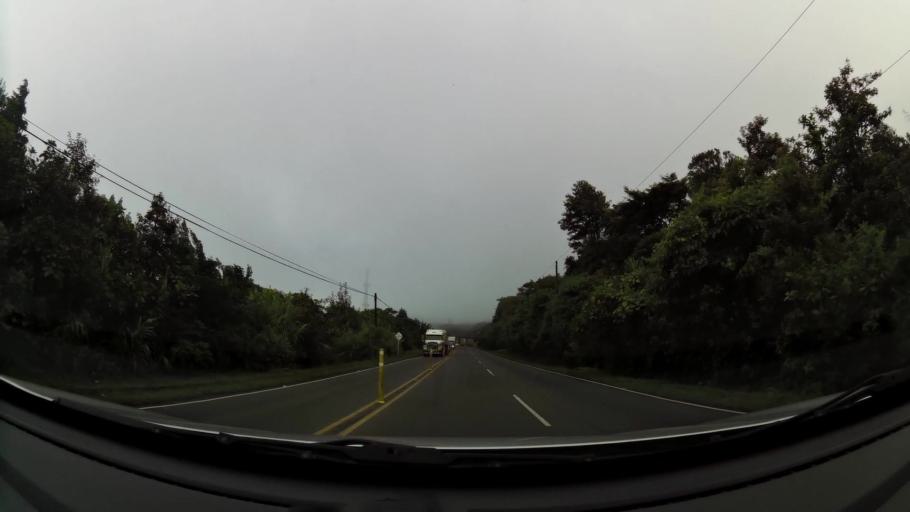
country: CR
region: Heredia
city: Angeles
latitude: 10.0447
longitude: -84.0054
